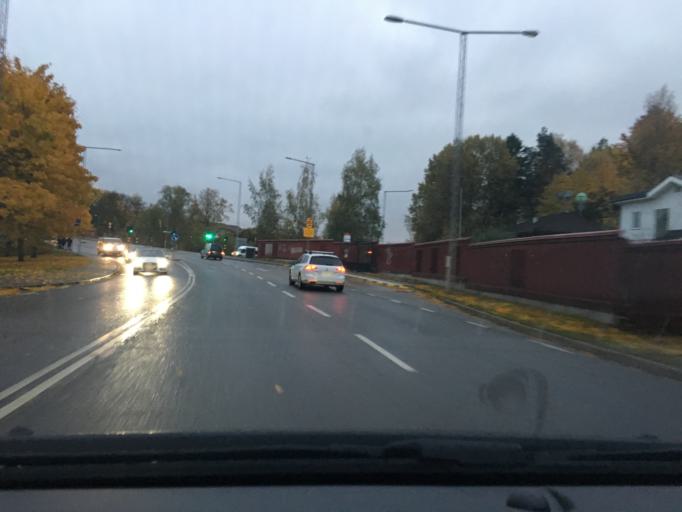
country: SE
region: Stockholm
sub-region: Stockholms Kommun
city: Bromma
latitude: 59.3730
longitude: 17.9189
